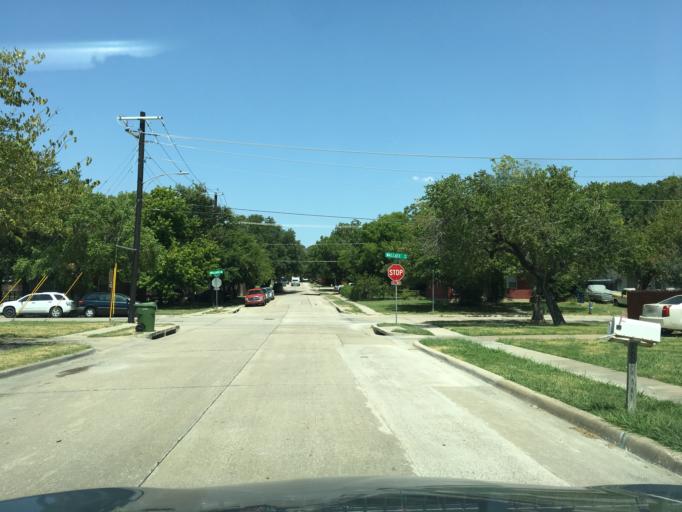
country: US
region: Texas
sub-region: Dallas County
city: Garland
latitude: 32.8921
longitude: -96.6259
